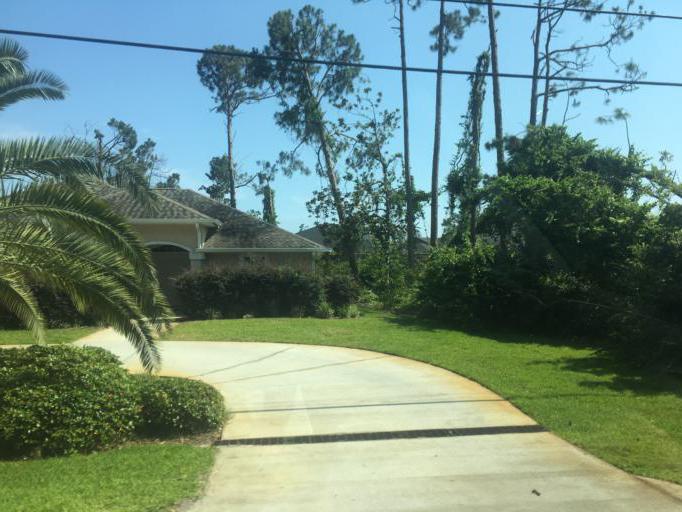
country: US
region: Florida
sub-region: Bay County
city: Upper Grand Lagoon
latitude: 30.1587
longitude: -85.7311
